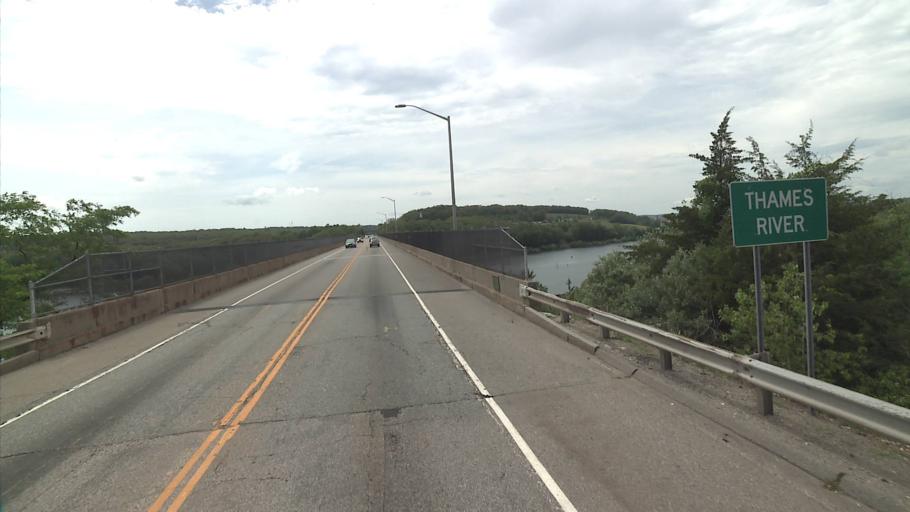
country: US
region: Connecticut
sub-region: New London County
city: Norwich
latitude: 41.4821
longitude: -72.0710
